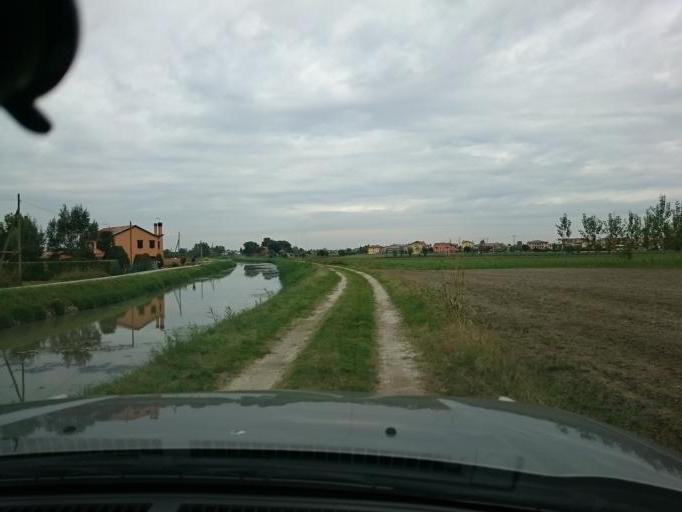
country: IT
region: Veneto
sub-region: Provincia di Padova
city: Codevigo
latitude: 45.2608
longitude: 12.0941
